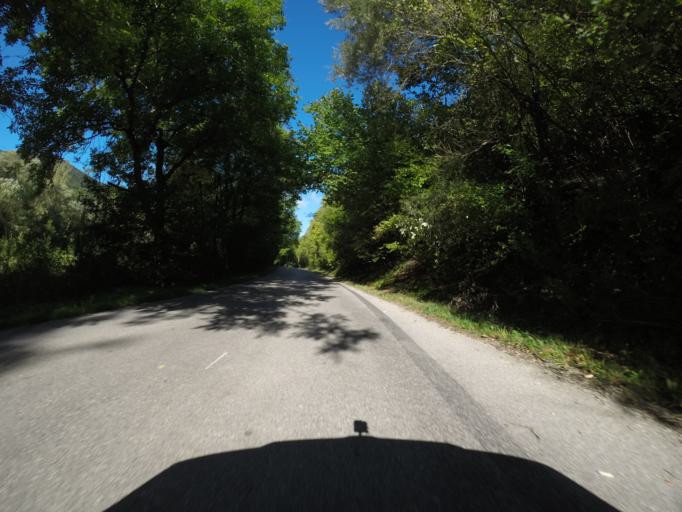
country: SK
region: Nitriansky
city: Ilava
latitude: 48.9679
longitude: 18.3566
